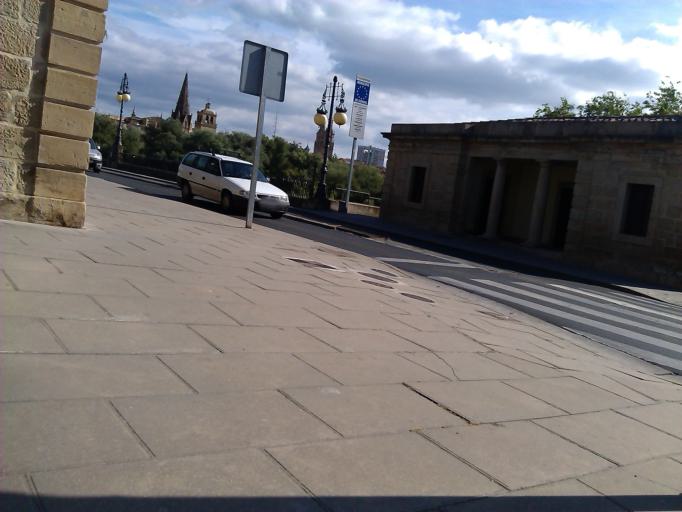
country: ES
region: La Rioja
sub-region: Provincia de La Rioja
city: Logrono
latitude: 42.4710
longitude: -2.4440
